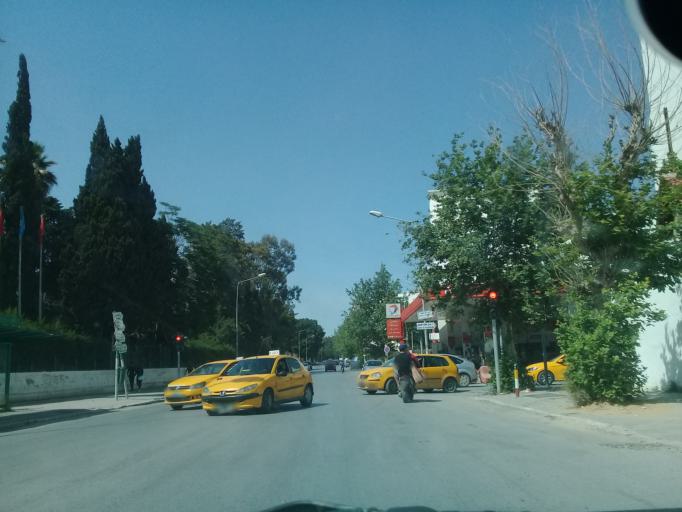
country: TN
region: Tunis
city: Tunis
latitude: 36.8138
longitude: 10.1752
